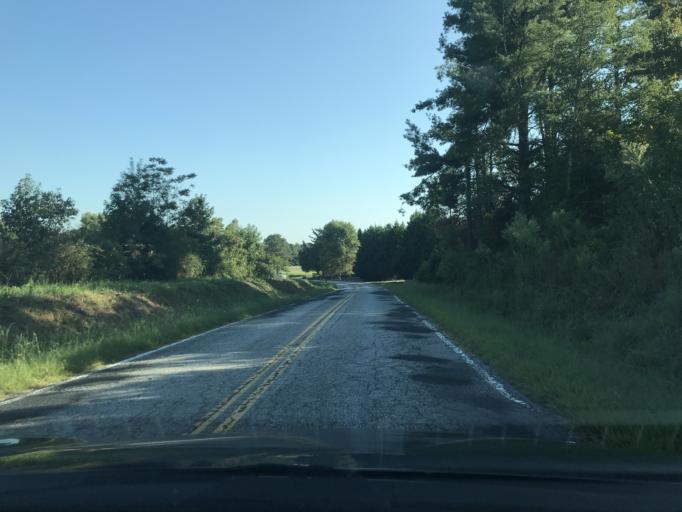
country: US
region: South Carolina
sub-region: Spartanburg County
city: Mayo
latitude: 35.1115
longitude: -81.7846
